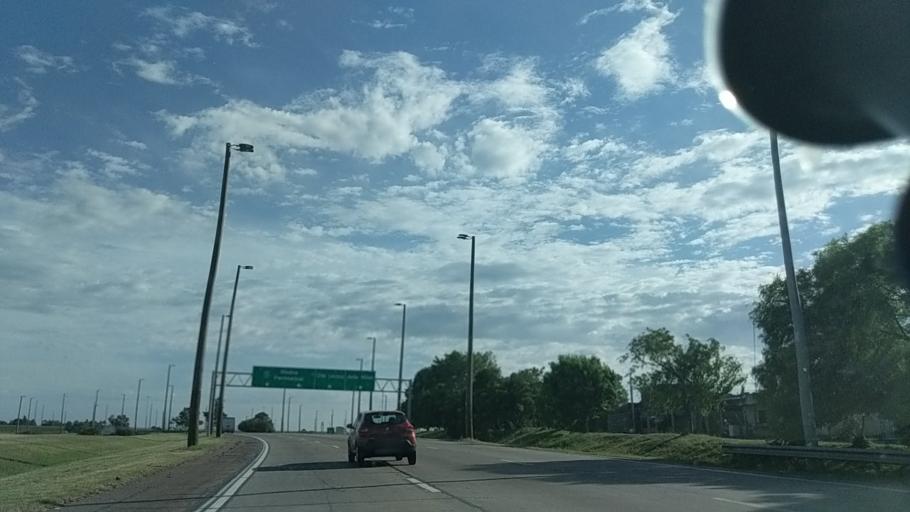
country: UY
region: Canelones
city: La Paz
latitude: -34.8292
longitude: -56.2510
